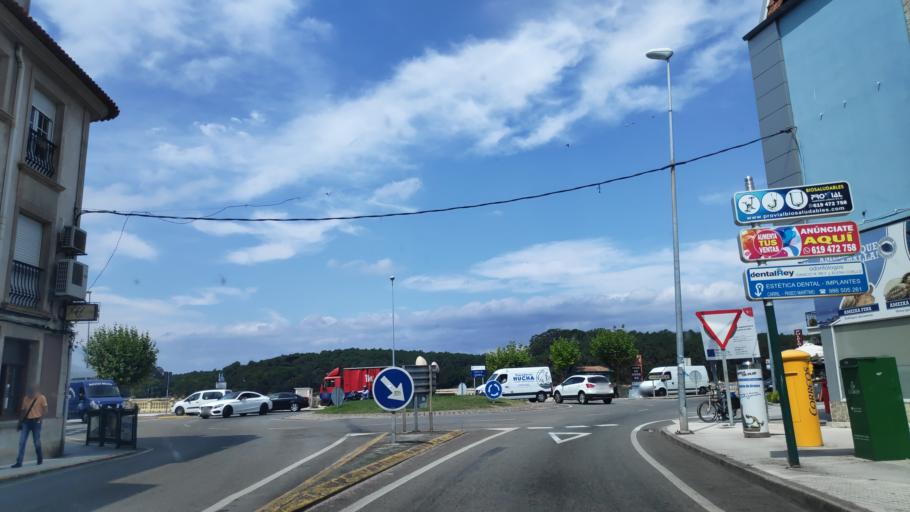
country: ES
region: Galicia
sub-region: Provincia de Pontevedra
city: Vilagarcia de Arousa
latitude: 42.6150
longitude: -8.7751
